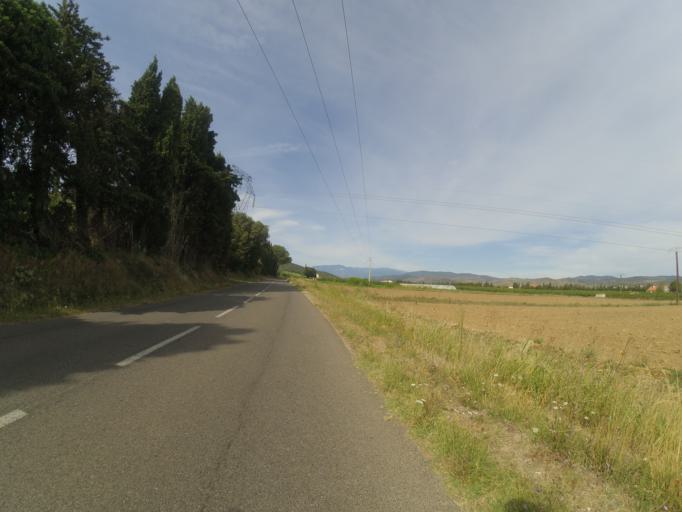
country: FR
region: Languedoc-Roussillon
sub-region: Departement des Pyrenees-Orientales
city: Ille-sur-Tet
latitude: 42.6572
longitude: 2.6391
